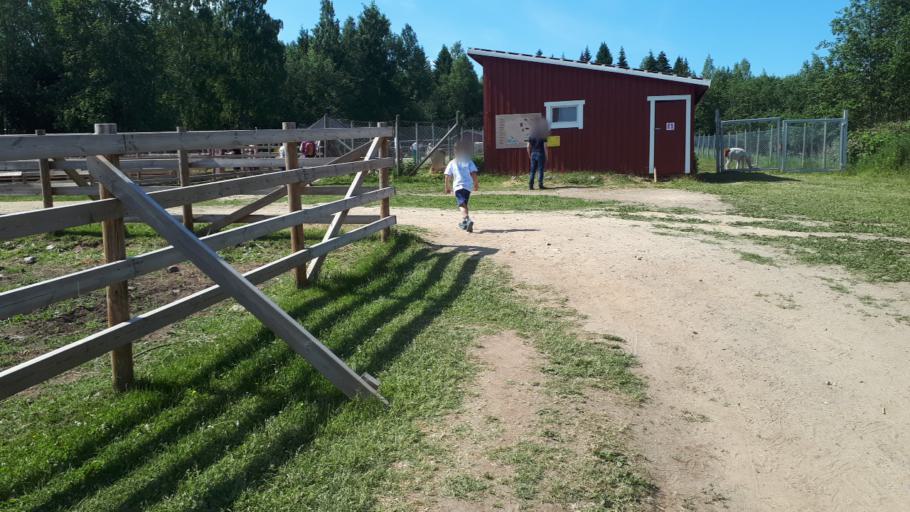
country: FI
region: Northern Savo
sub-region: Kuopio
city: Kuopio
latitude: 62.7519
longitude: 27.5519
